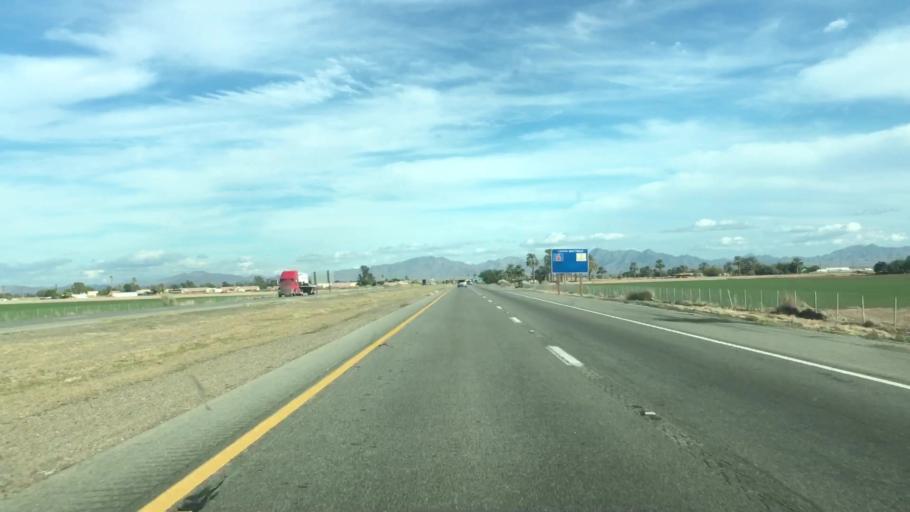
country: US
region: California
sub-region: Riverside County
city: Blythe
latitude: 33.6066
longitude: -114.6366
